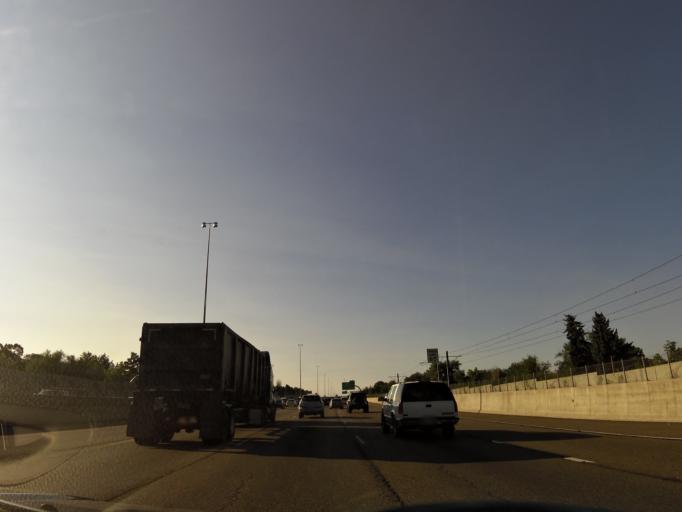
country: US
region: Colorado
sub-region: Arapahoe County
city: Cherry Hills Village
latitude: 39.6636
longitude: -104.9234
